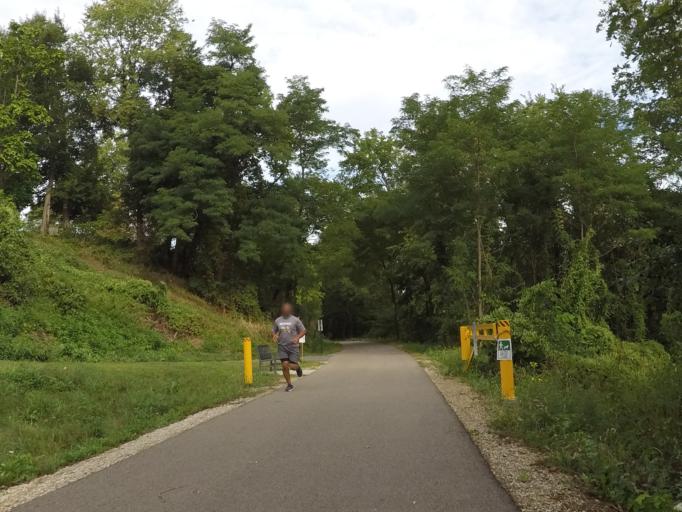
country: US
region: Wisconsin
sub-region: Sauk County
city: Prairie du Sac
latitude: 43.2955
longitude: -89.7249
